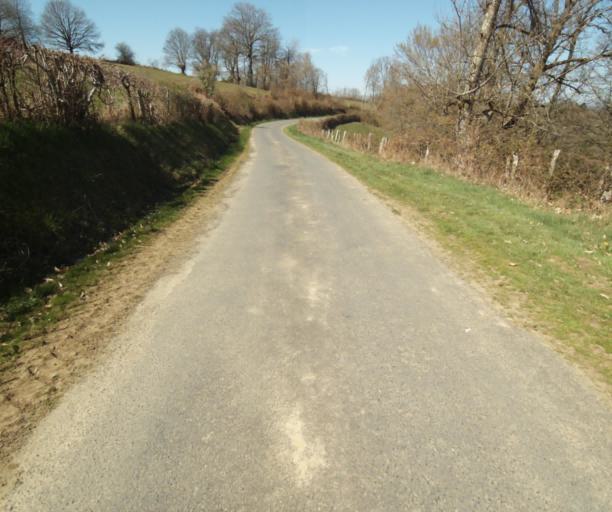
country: FR
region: Limousin
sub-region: Departement de la Correze
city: Chamboulive
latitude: 45.4404
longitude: 1.6849
